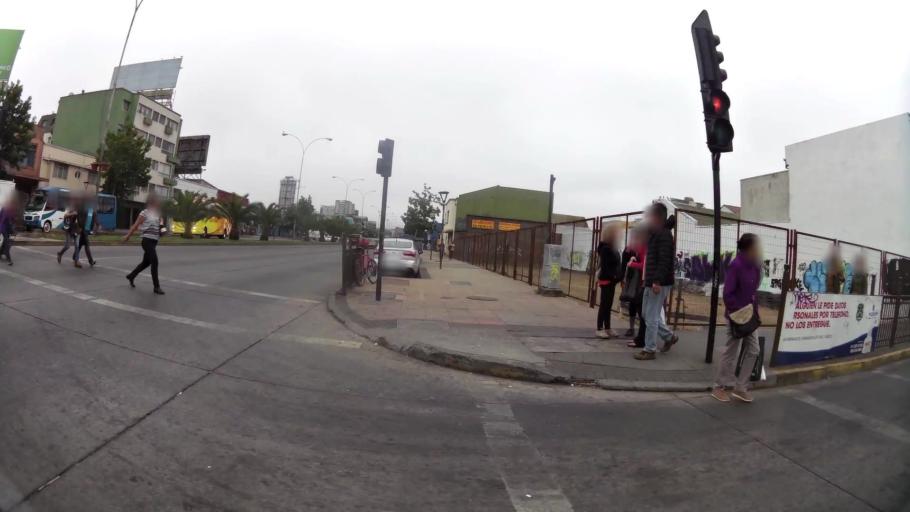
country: CL
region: Biobio
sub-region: Provincia de Concepcion
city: Concepcion
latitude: -36.8218
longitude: -73.0480
